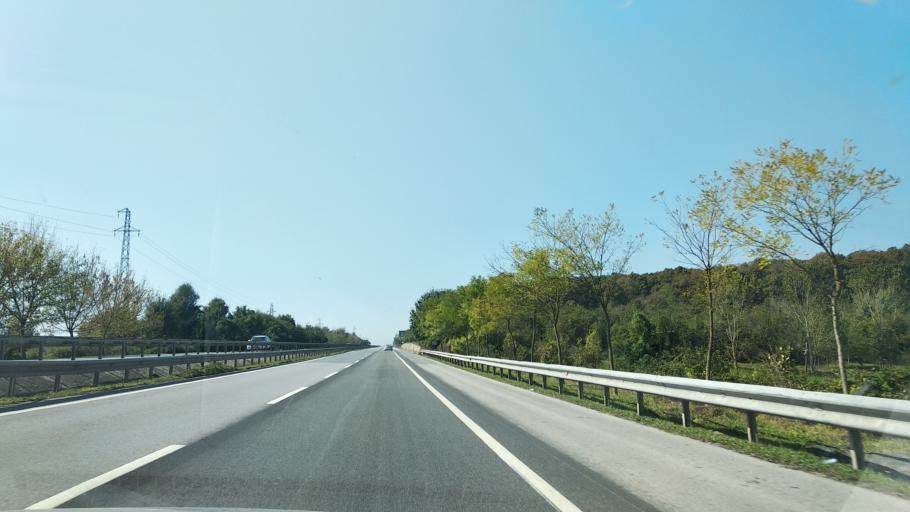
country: TR
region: Kocaeli
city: Derbent
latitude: 40.7317
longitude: 30.1717
